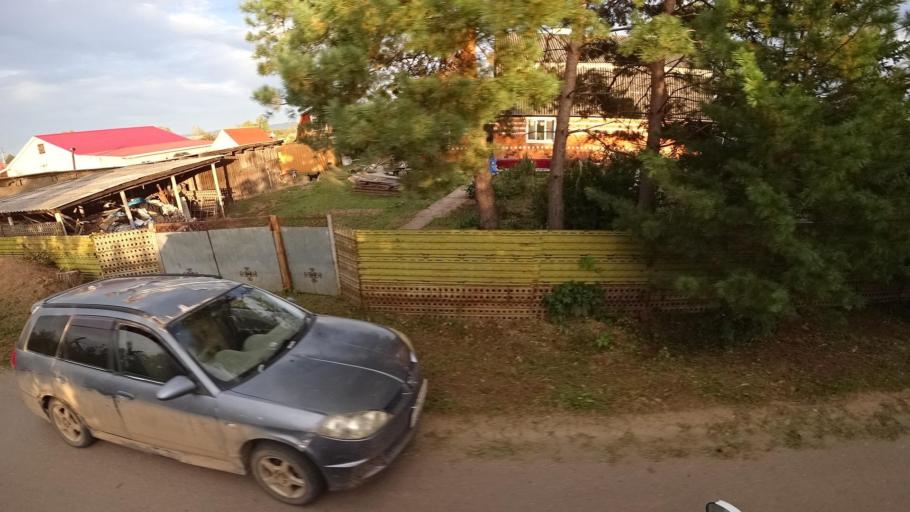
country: RU
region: Primorskiy
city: Yakovlevka
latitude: 44.4266
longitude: 133.4820
